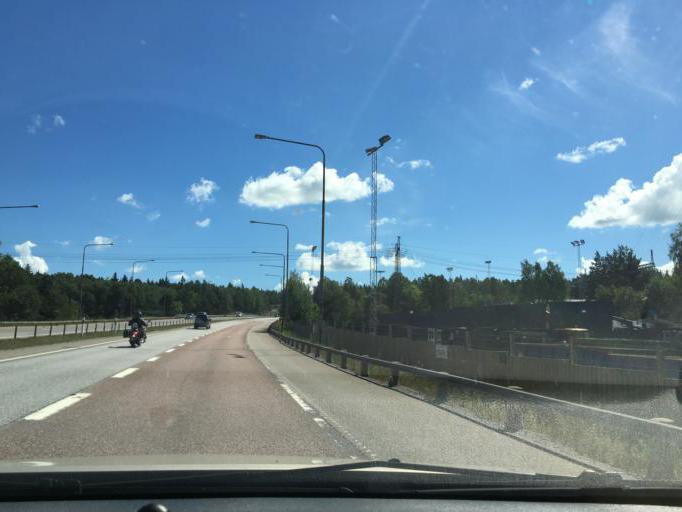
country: SE
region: Stockholm
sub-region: Nacka Kommun
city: Fisksatra
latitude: 59.2924
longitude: 18.2346
